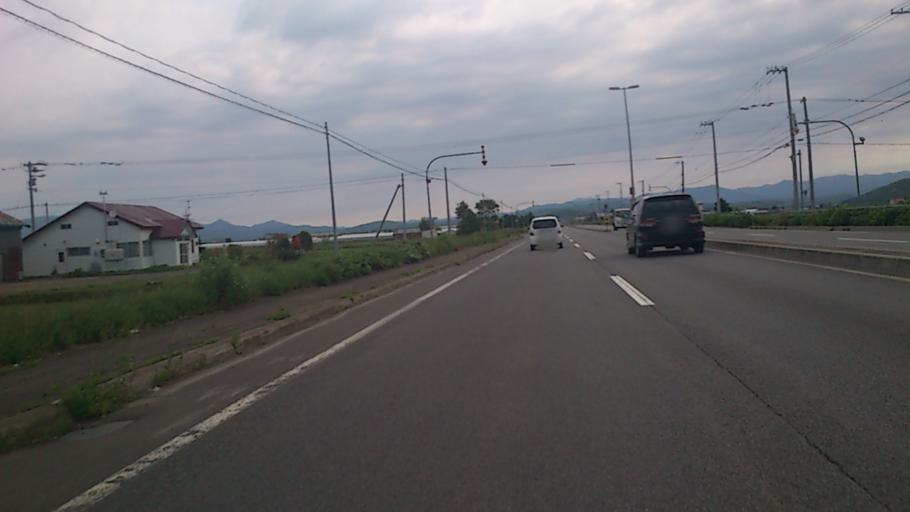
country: JP
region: Hokkaido
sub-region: Asahikawa-shi
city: Asahikawa
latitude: 43.8478
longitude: 142.4935
